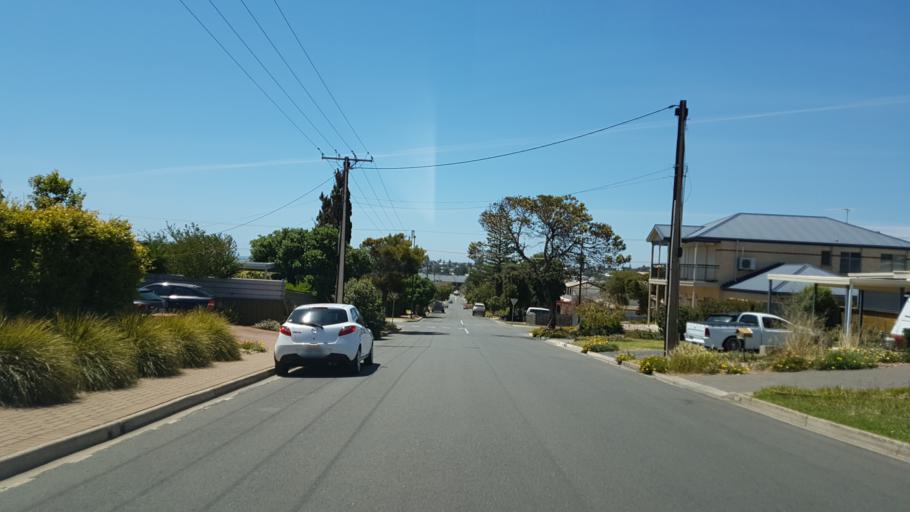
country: AU
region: South Australia
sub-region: Onkaparinga
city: Moana
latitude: -35.2095
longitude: 138.4734
